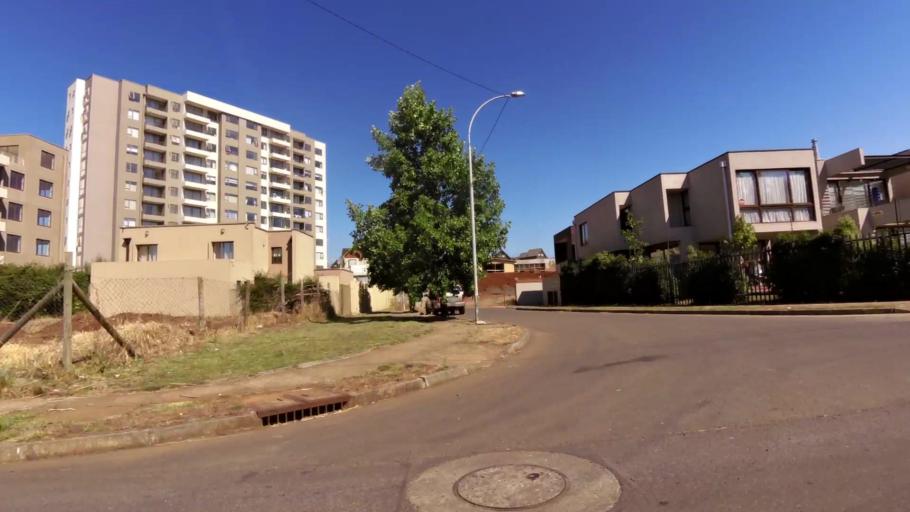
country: CL
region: Biobio
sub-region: Provincia de Concepcion
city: Concepcion
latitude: -36.7839
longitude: -73.0477
